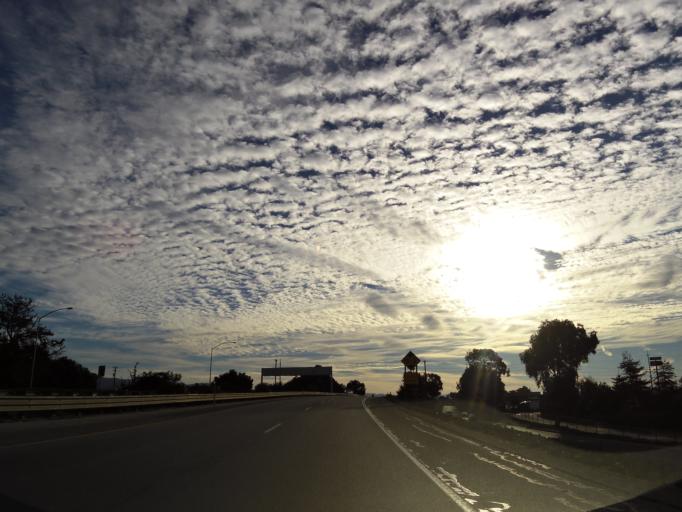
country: US
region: California
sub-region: Monterey County
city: Salinas
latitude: 36.6673
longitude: -121.6301
